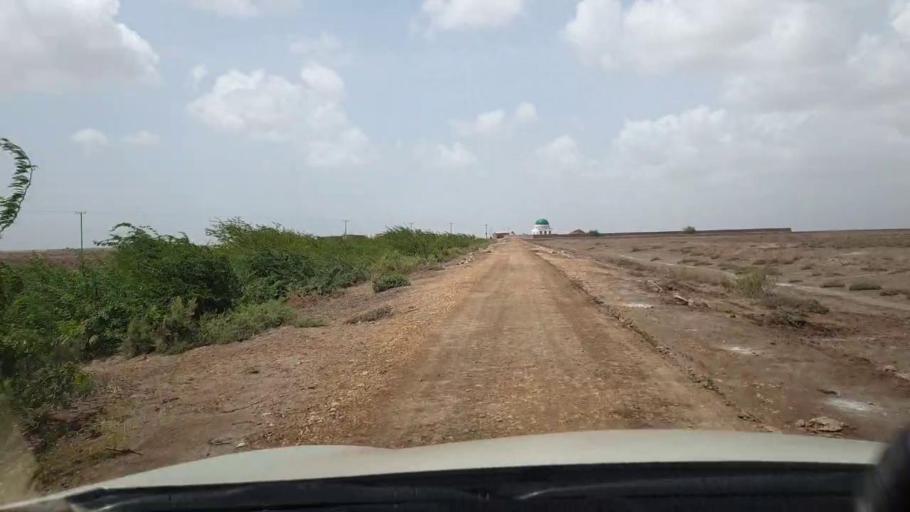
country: PK
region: Sindh
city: Kadhan
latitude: 24.3632
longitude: 68.8478
